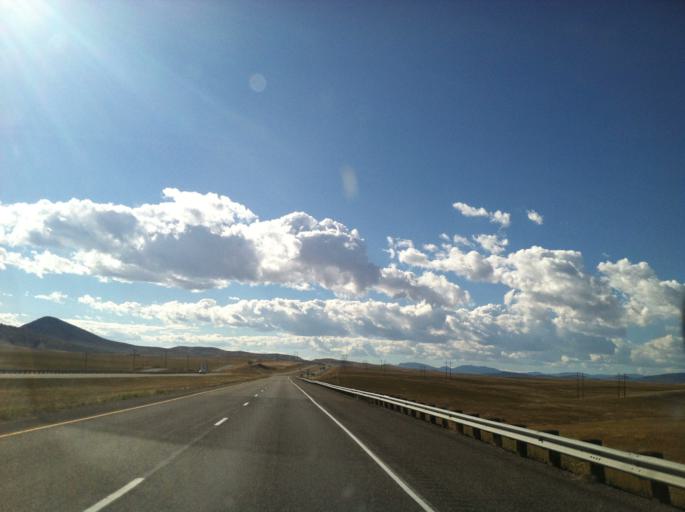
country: US
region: Montana
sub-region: Gallatin County
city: Three Forks
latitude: 45.9185
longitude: -111.6086
